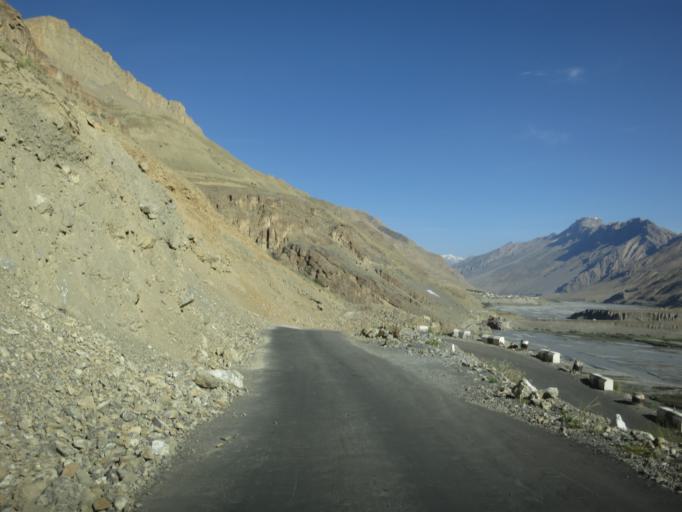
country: IN
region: Himachal Pradesh
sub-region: Shimla
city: Sarahan
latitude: 32.2556
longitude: 78.0464
